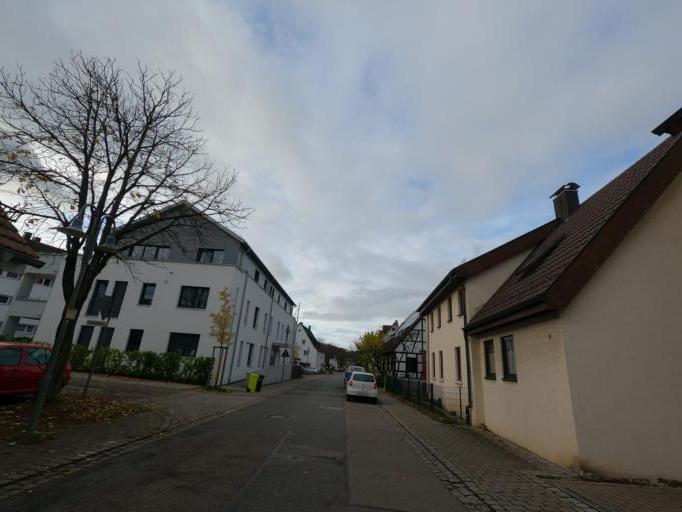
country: DE
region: Baden-Wuerttemberg
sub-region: Regierungsbezirk Stuttgart
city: Uhingen
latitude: 48.7046
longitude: 9.5894
